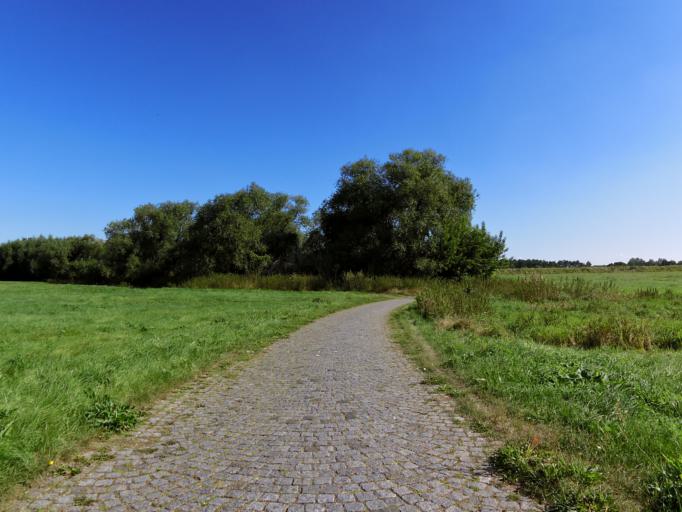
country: DE
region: Saxony
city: Riesa
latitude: 51.3390
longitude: 13.2934
